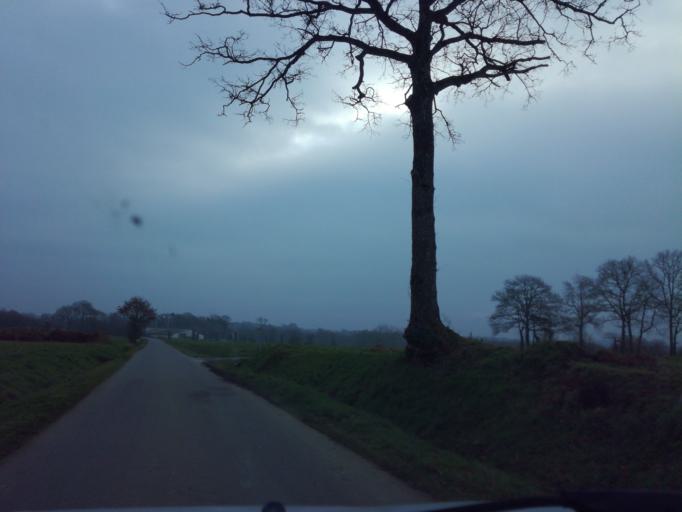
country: FR
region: Brittany
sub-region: Departement d'Ille-et-Vilaine
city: Gosne
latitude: 48.2609
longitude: -1.4633
